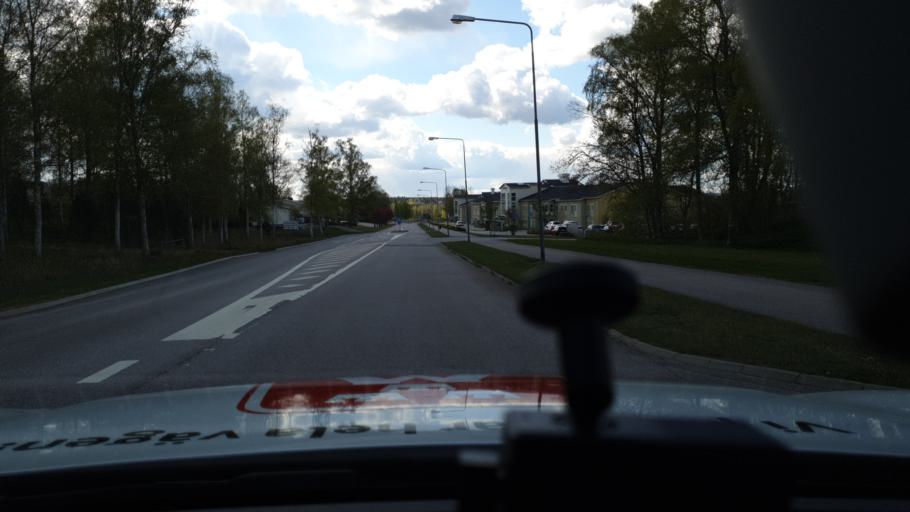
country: SE
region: Kalmar
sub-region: Vimmerby Kommun
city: Vimmerby
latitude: 57.6677
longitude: 15.8747
